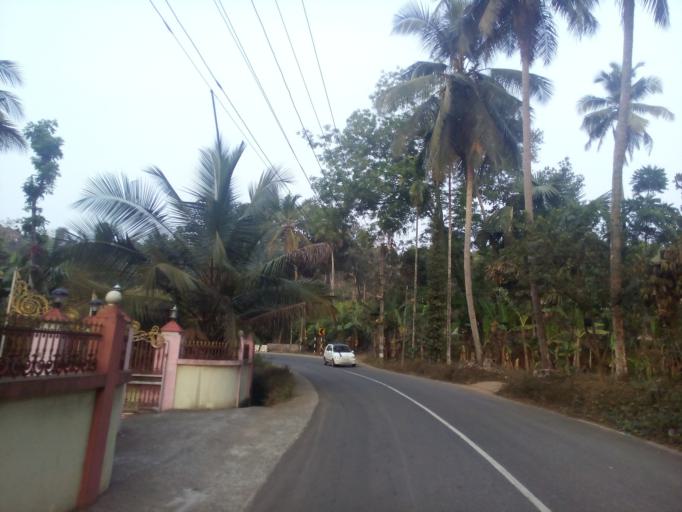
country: IN
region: Kerala
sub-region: Kottayam
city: Palackattumala
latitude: 9.8123
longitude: 76.6678
